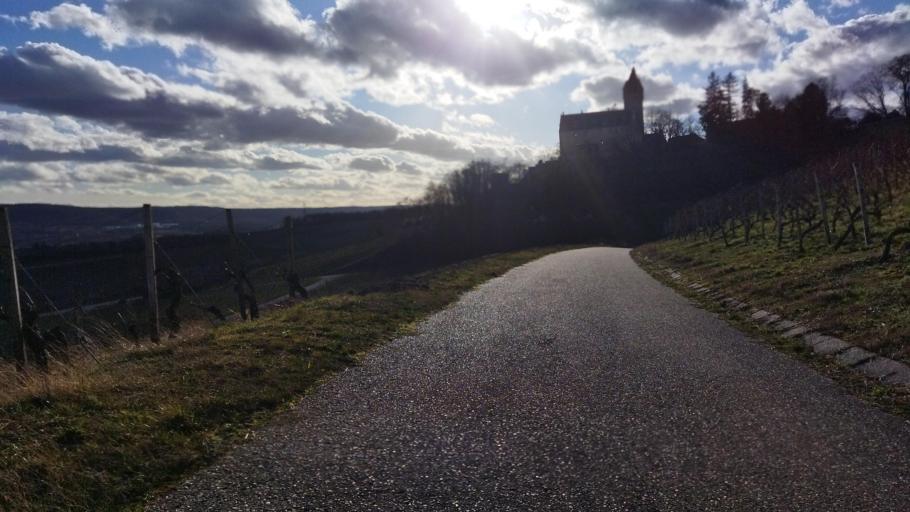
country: DE
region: Baden-Wuerttemberg
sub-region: Regierungsbezirk Stuttgart
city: Guglingen
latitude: 49.0897
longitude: 9.0124
